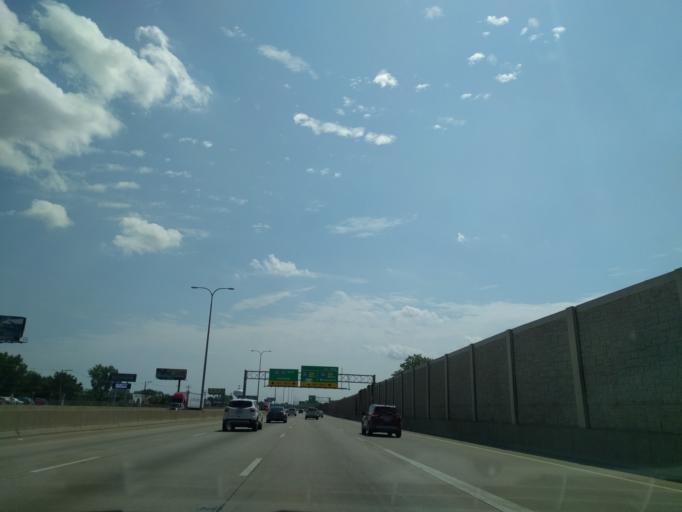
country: US
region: Illinois
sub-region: Cook County
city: South Holland
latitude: 41.5974
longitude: -87.5837
